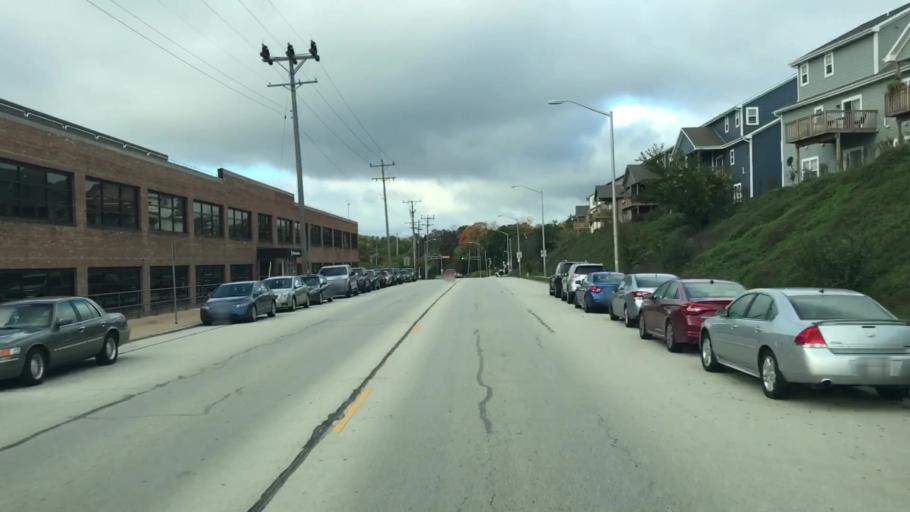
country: US
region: Wisconsin
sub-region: Waukesha County
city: Waukesha
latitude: 43.0057
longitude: -88.2488
